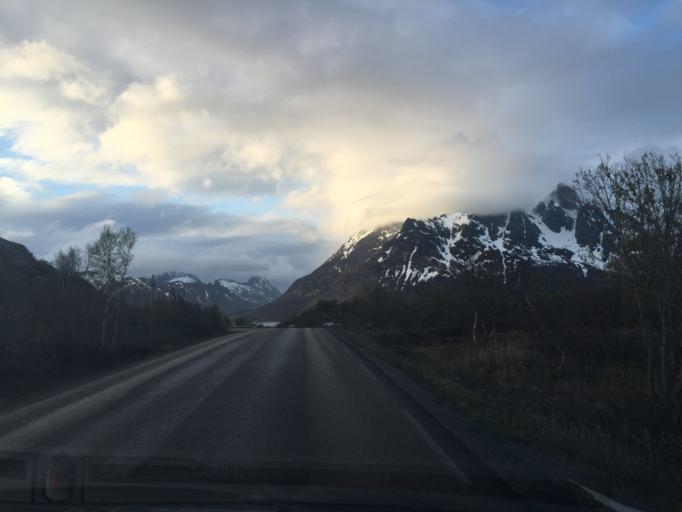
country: NO
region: Nordland
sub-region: Vagan
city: Svolvaer
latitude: 68.3139
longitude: 14.7129
